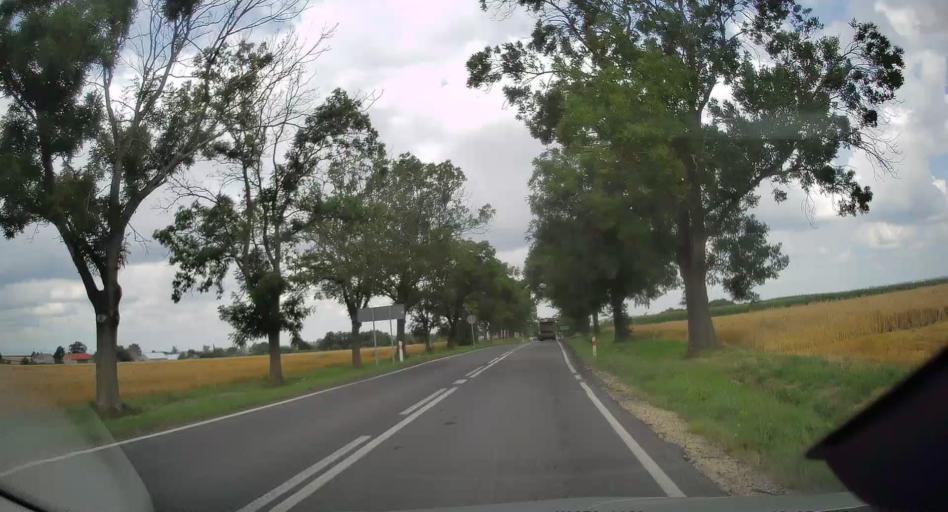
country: PL
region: Opole Voivodeship
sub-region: Powiat prudnicki
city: Glogowek
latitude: 50.3394
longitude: 17.9168
